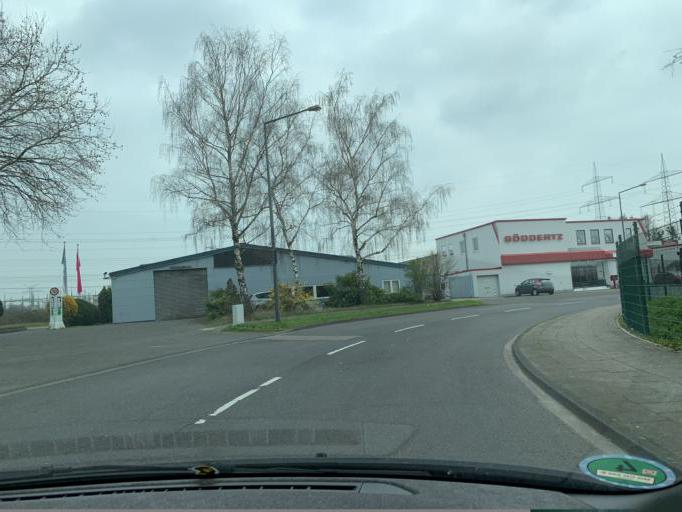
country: DE
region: North Rhine-Westphalia
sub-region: Regierungsbezirk Koln
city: Leverkusen
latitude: 51.0355
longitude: 6.9296
